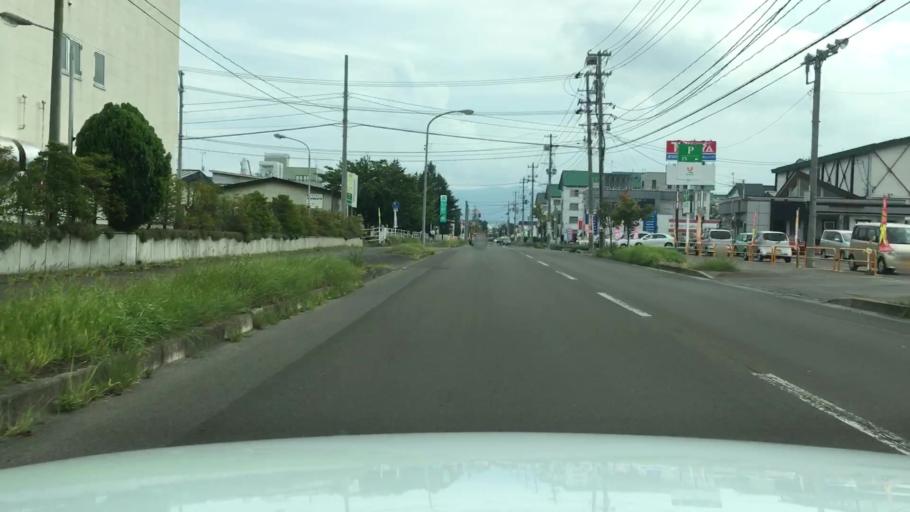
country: JP
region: Aomori
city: Hirosaki
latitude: 40.6220
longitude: 140.4849
